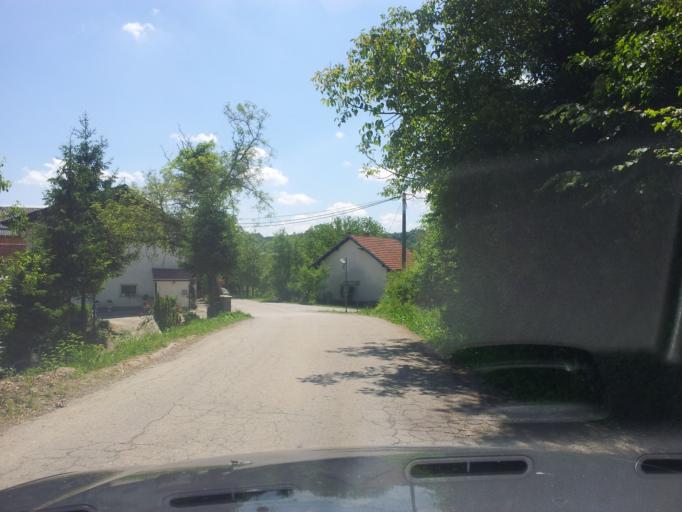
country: HR
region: Karlovacka
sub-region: Grad Karlovac
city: Karlovac
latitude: 45.4759
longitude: 15.4576
